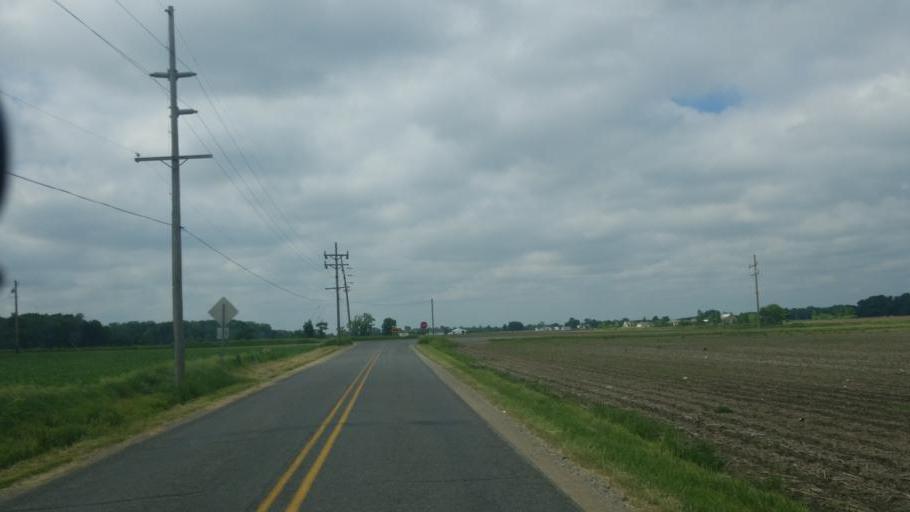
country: US
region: Indiana
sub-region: Elkhart County
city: Wakarusa
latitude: 41.4926
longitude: -86.0258
